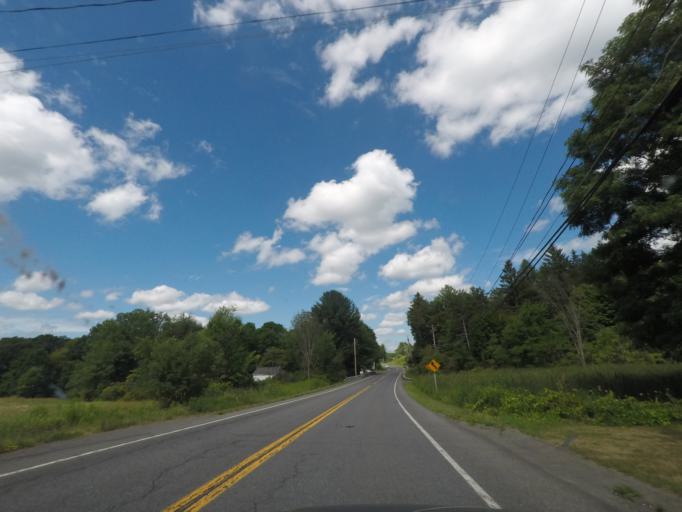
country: US
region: New York
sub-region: Rensselaer County
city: West Sand Lake
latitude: 42.6151
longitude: -73.6354
